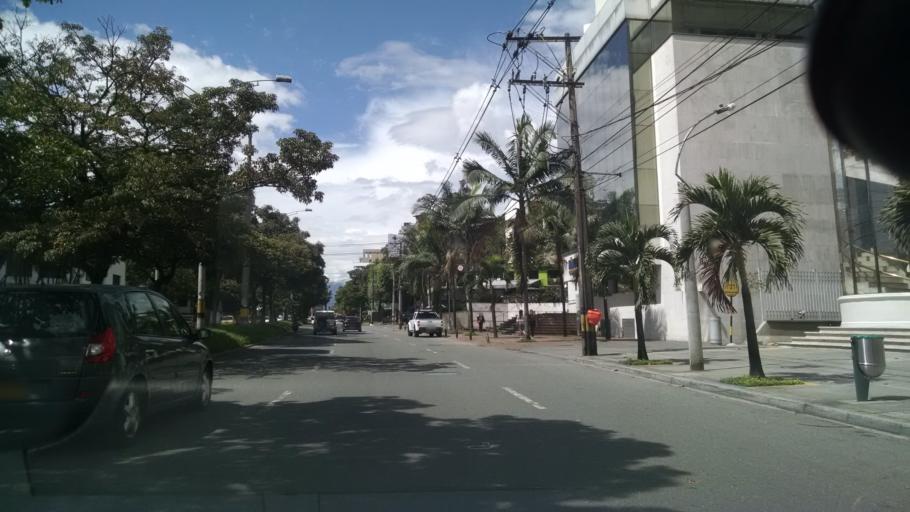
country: CO
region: Antioquia
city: Itagui
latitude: 6.2119
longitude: -75.5700
